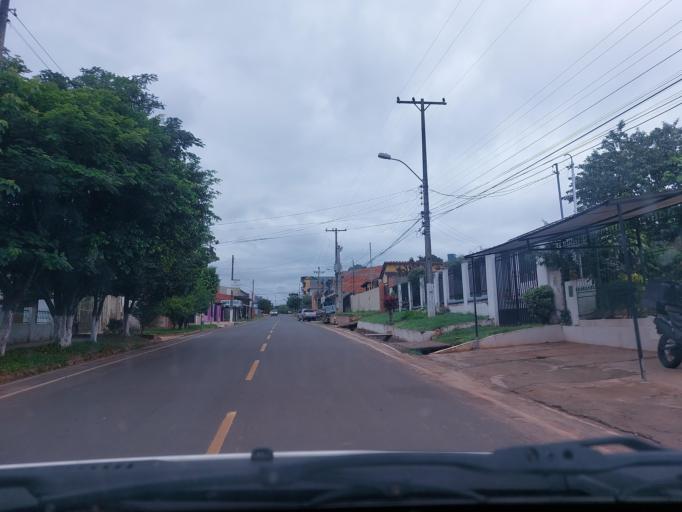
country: PY
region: San Pedro
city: Guayaybi
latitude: -24.6610
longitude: -56.4398
